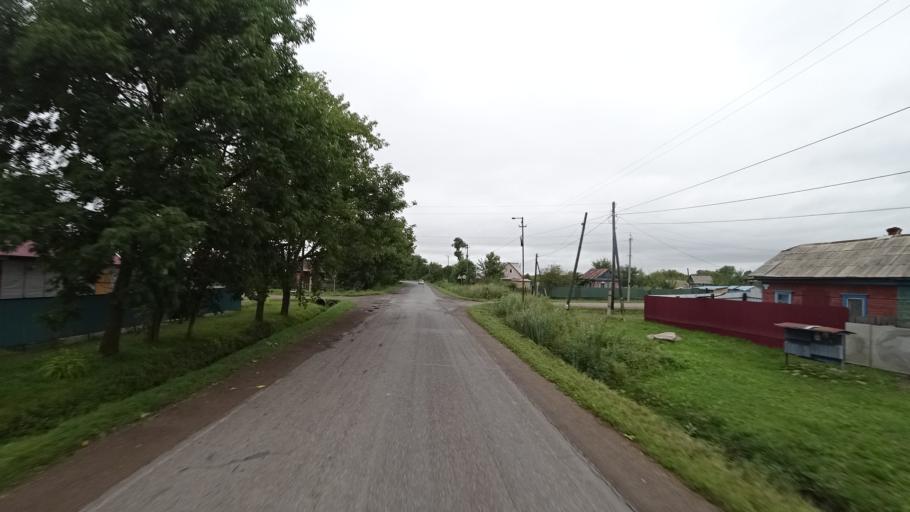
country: RU
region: Primorskiy
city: Chernigovka
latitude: 44.3471
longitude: 132.5641
